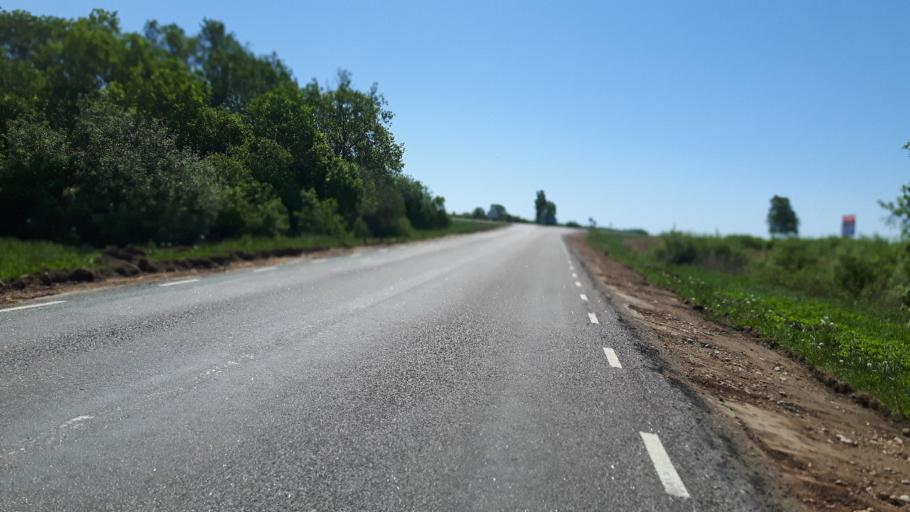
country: EE
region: Ida-Virumaa
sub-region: Narva-Joesuu linn
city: Narva-Joesuu
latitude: 59.3803
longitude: 27.9215
